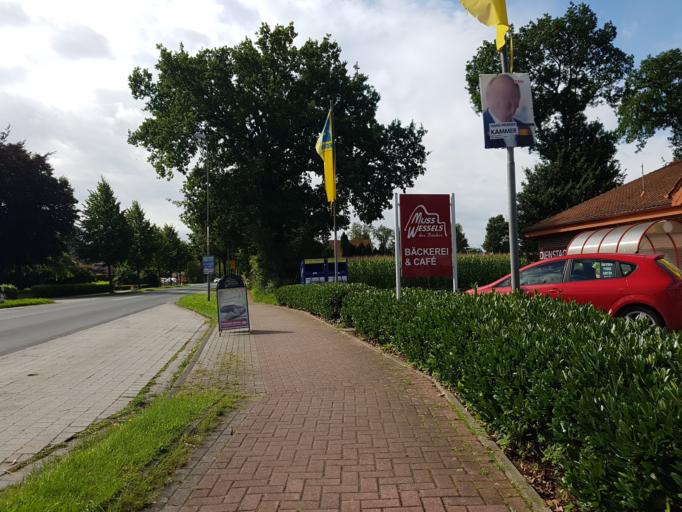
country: DE
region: Lower Saxony
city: Wittmund
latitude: 53.5286
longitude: 7.7814
